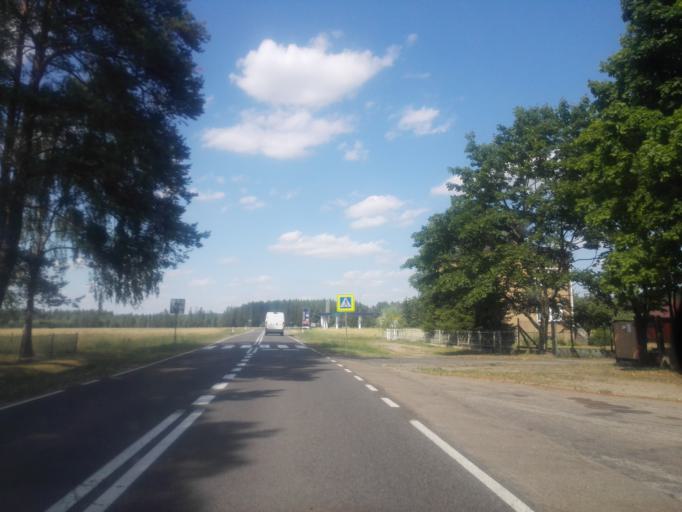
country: PL
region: Podlasie
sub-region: Powiat sejnenski
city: Sejny
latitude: 53.9807
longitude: 23.2936
